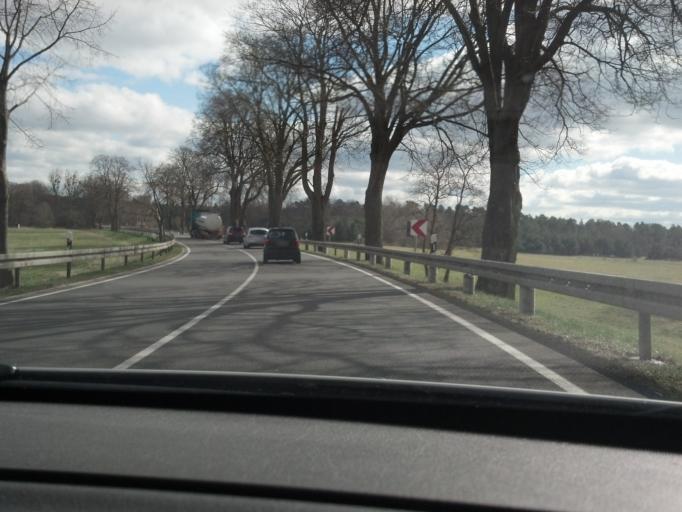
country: DE
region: Mecklenburg-Vorpommern
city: Neustrelitz
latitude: 53.3116
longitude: 13.0998
